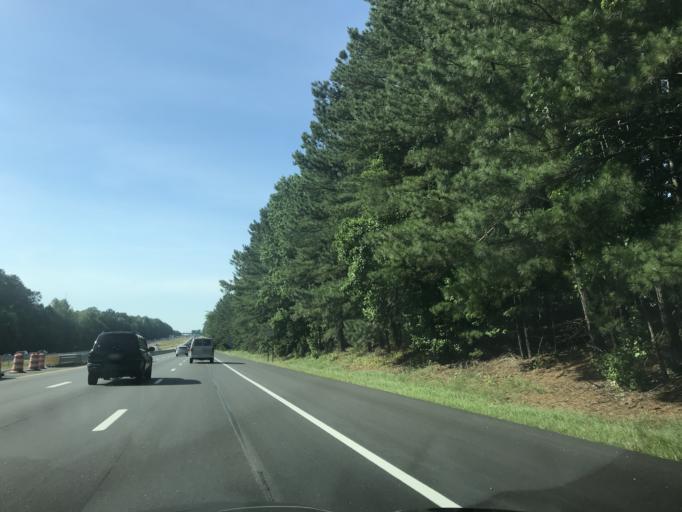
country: US
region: North Carolina
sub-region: Wake County
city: Garner
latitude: 35.7356
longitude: -78.5887
